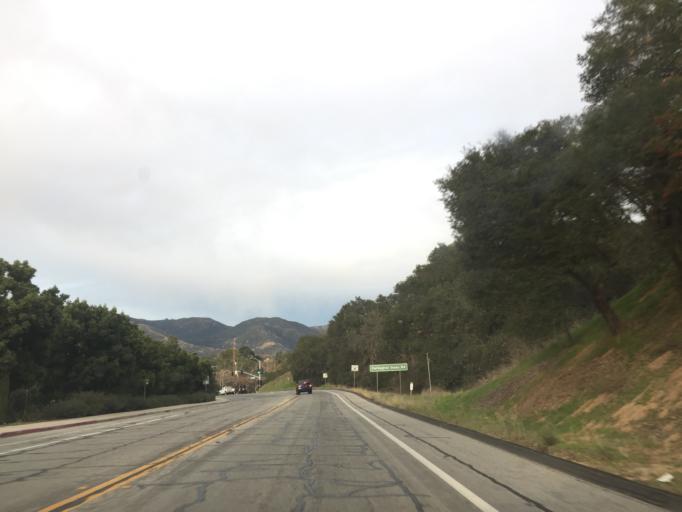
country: US
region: California
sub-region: Santa Barbara County
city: Goleta
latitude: 34.4499
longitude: -119.7909
